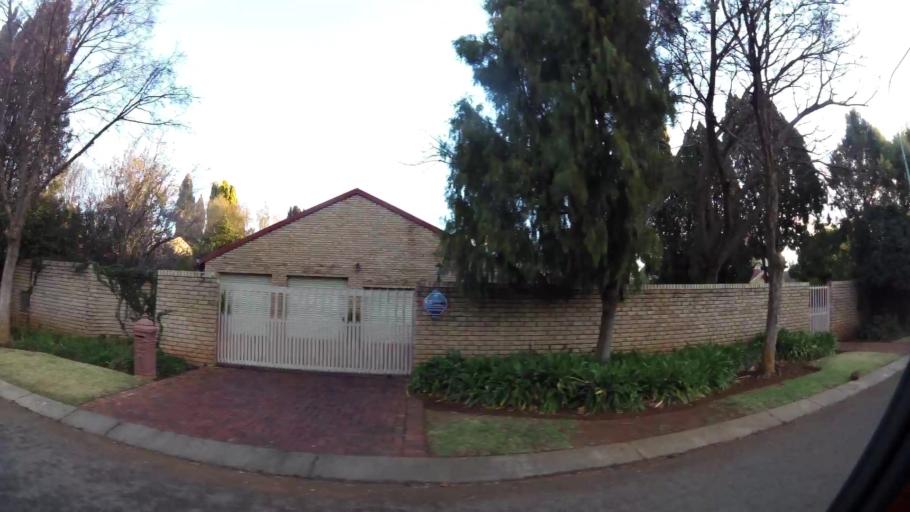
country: ZA
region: North-West
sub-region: Dr Kenneth Kaunda District Municipality
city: Potchefstroom
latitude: -26.6779
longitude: 27.1090
